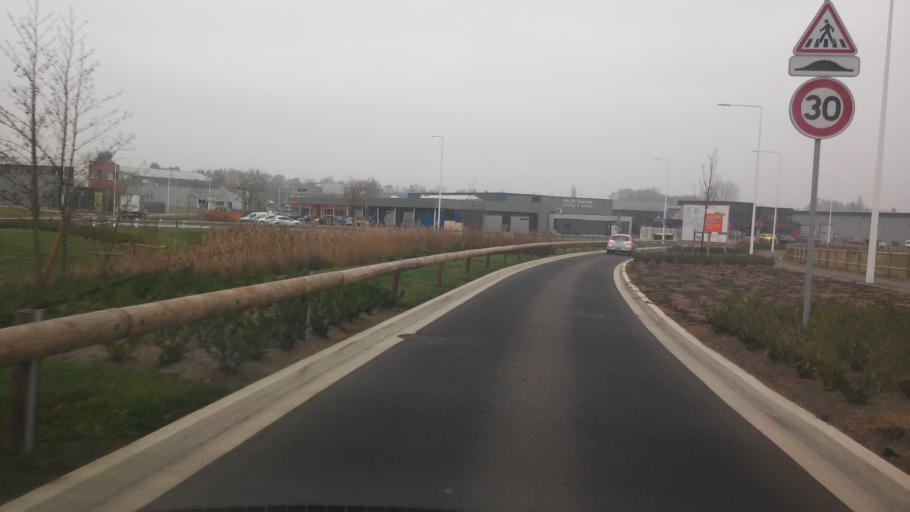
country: FR
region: Lorraine
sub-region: Departement de la Moselle
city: Marly
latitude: 49.0650
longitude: 6.1391
